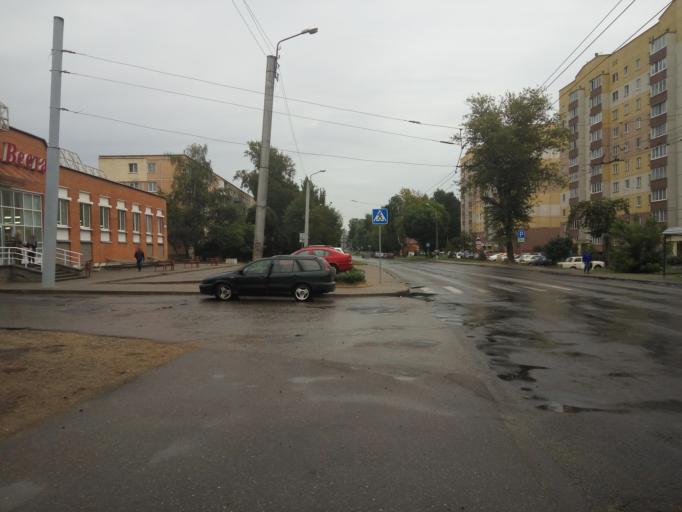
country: BY
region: Vitebsk
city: Vitebsk
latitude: 55.2002
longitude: 30.2491
